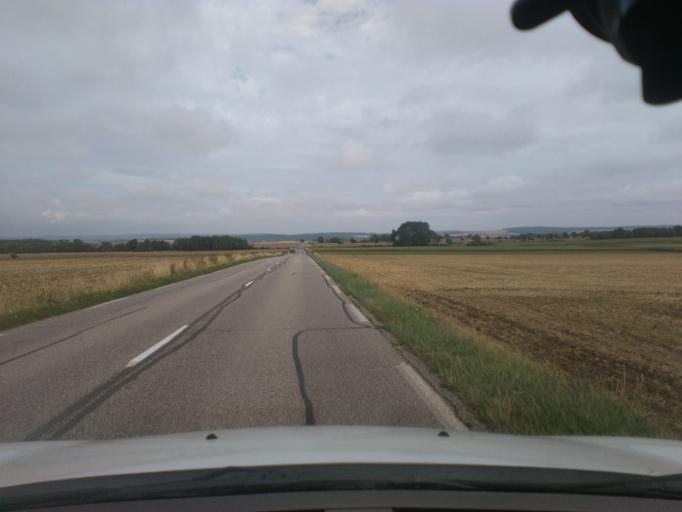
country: FR
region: Lorraine
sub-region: Departement de Meurthe-et-Moselle
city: Vezelise
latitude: 48.4817
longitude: 6.1423
